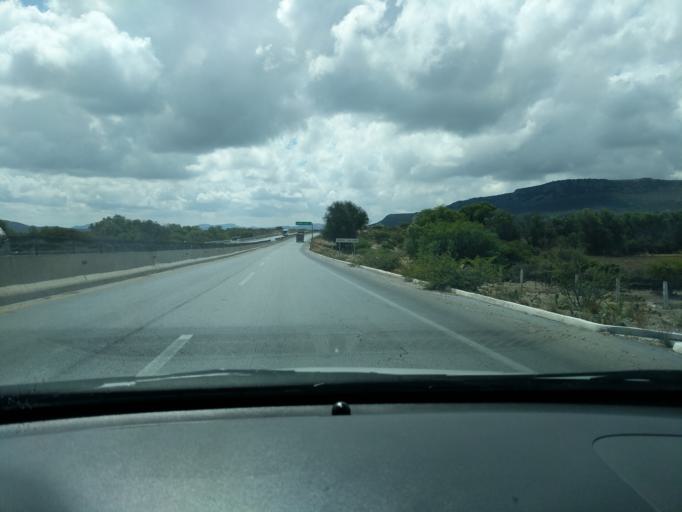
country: MX
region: Zacatecas
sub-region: Pinos
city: Santiago
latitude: 22.4069
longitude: -101.3939
